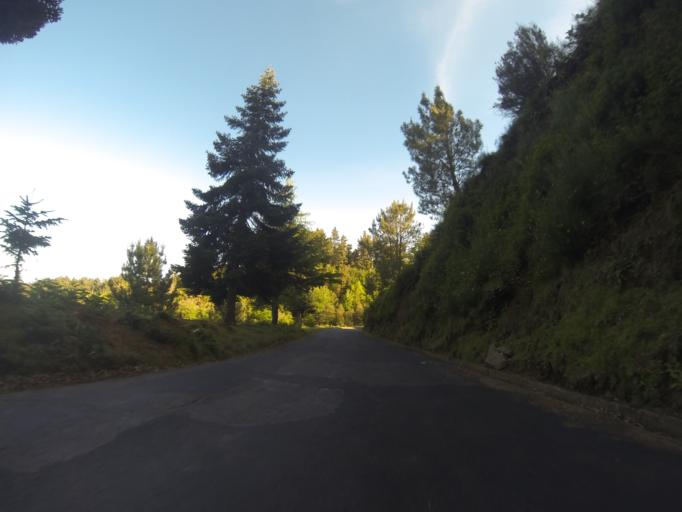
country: PT
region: Madeira
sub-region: Funchal
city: Nossa Senhora do Monte
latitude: 32.6976
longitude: -16.8825
